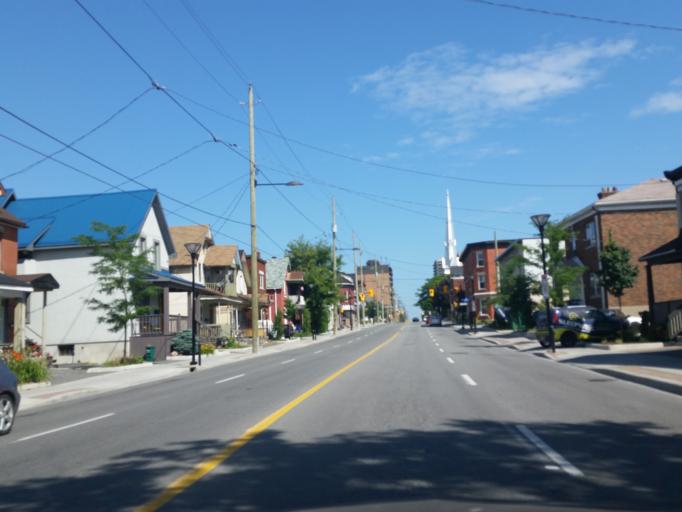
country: CA
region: Ontario
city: Ottawa
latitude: 45.4086
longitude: -75.7041
